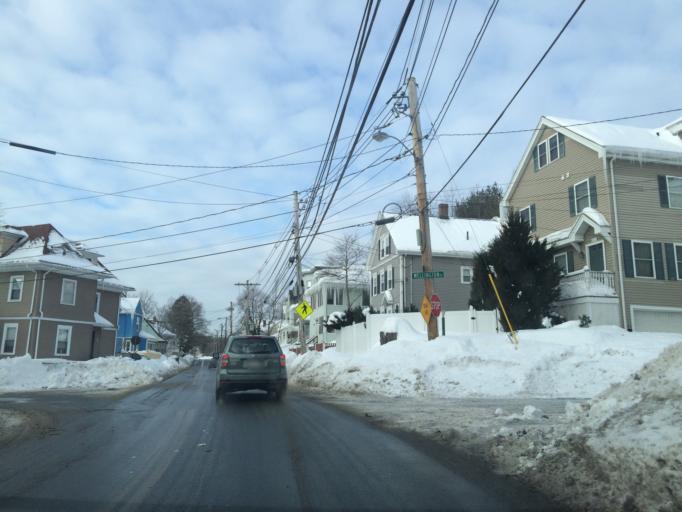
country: US
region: Massachusetts
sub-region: Middlesex County
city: Waltham
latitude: 42.3786
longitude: -71.2482
